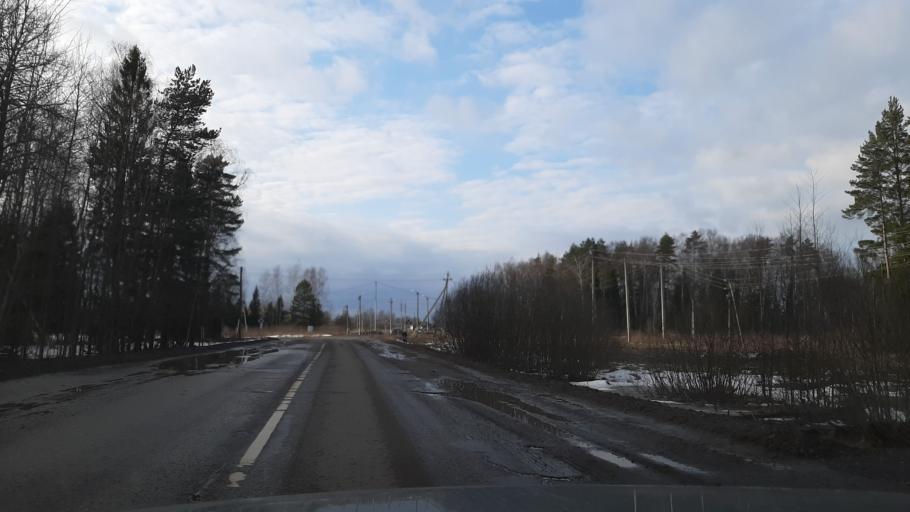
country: RU
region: Ivanovo
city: Novo-Talitsy
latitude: 56.9377
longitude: 40.7243
